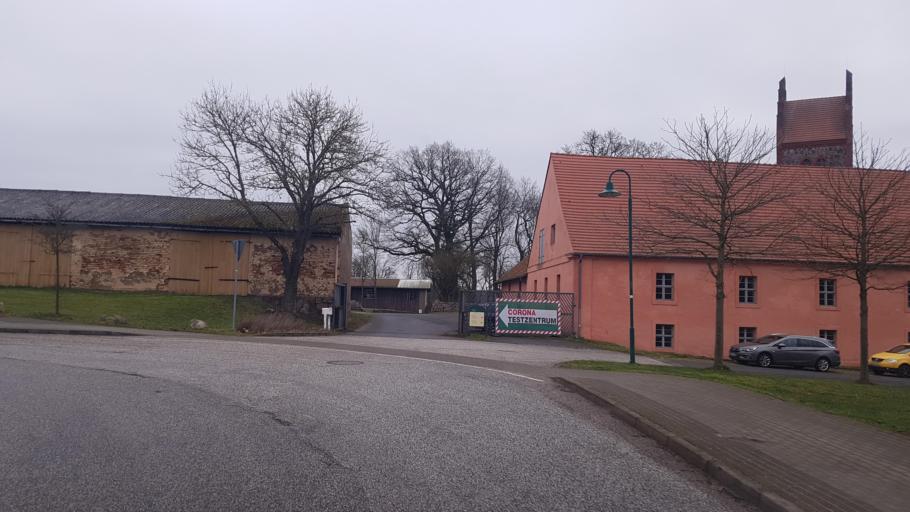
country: DE
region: Brandenburg
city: Zehdenick
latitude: 52.8949
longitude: 13.2568
